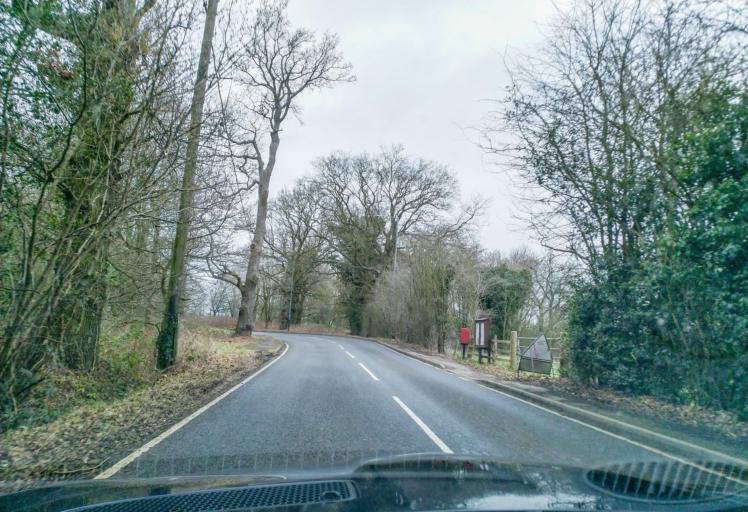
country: GB
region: England
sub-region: Warwickshire
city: Wroxall
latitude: 52.3278
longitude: -1.6671
